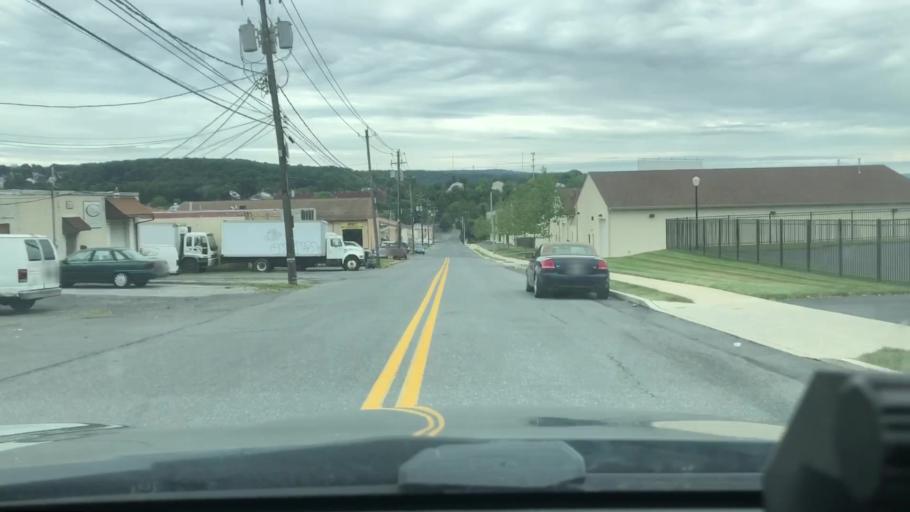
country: US
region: Pennsylvania
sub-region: Lehigh County
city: Fullerton
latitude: 40.6224
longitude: -75.4490
